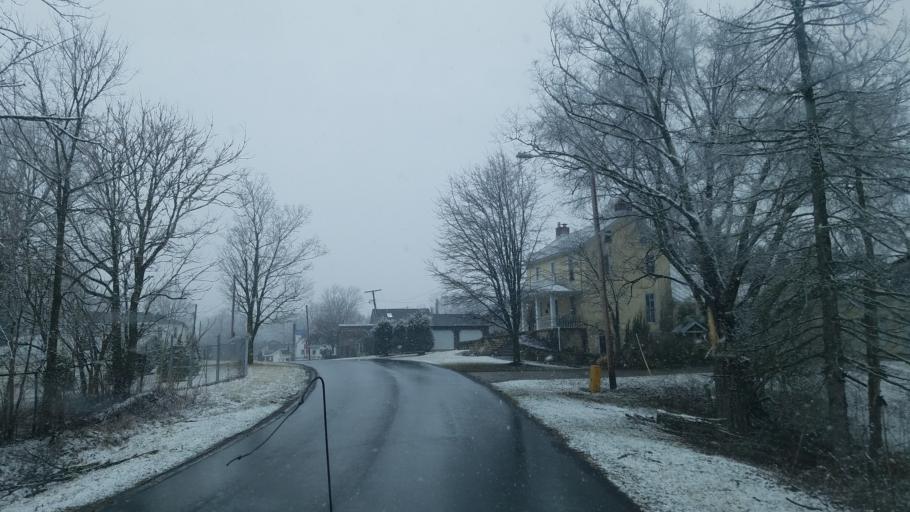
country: US
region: Ohio
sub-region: Logan County
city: Bellefontaine
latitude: 40.3368
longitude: -83.6760
